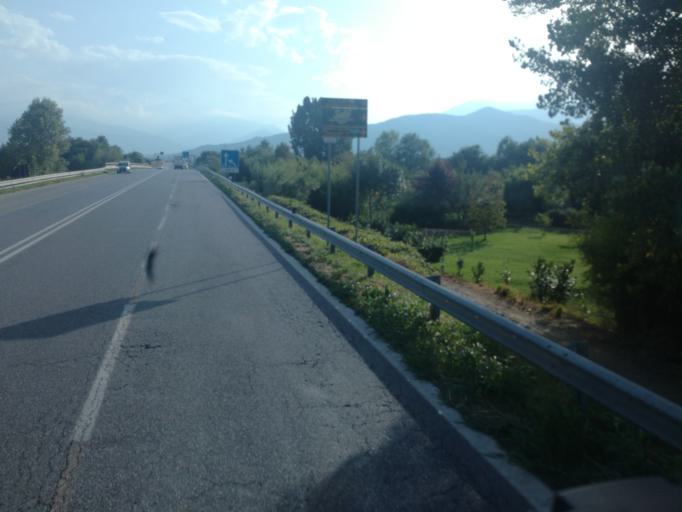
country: IT
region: Piedmont
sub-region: Provincia di Torino
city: Pinerolo
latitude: 44.8679
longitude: 7.3377
